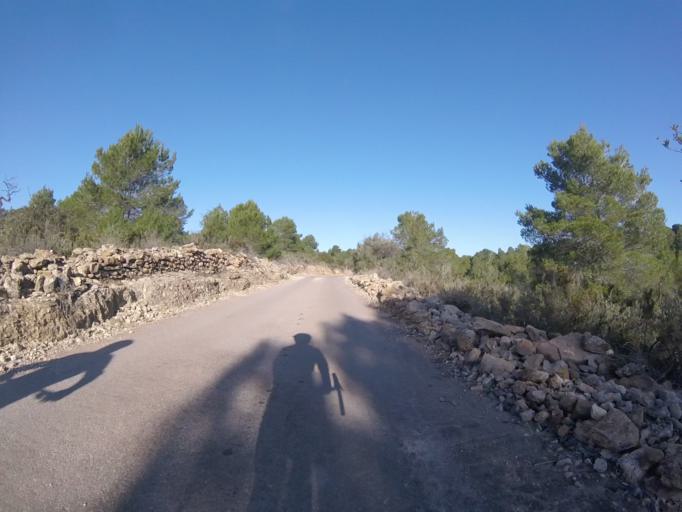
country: ES
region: Valencia
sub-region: Provincia de Castello
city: Alcala de Xivert
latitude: 40.2704
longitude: 0.2069
